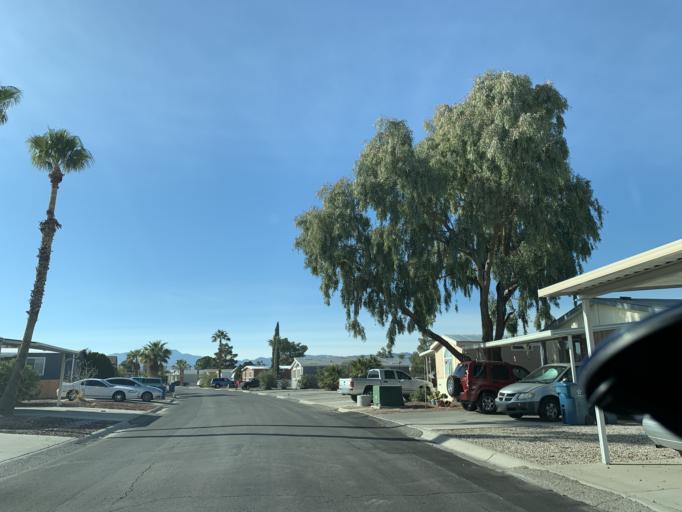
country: US
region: Nevada
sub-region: Clark County
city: Spring Valley
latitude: 36.1026
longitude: -115.2272
